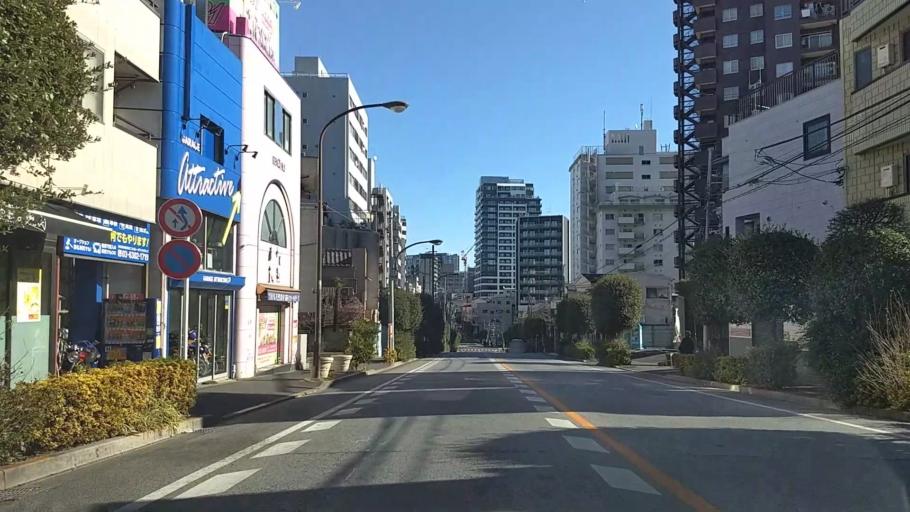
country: JP
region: Tokyo
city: Tokyo
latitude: 35.6996
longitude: 139.7242
